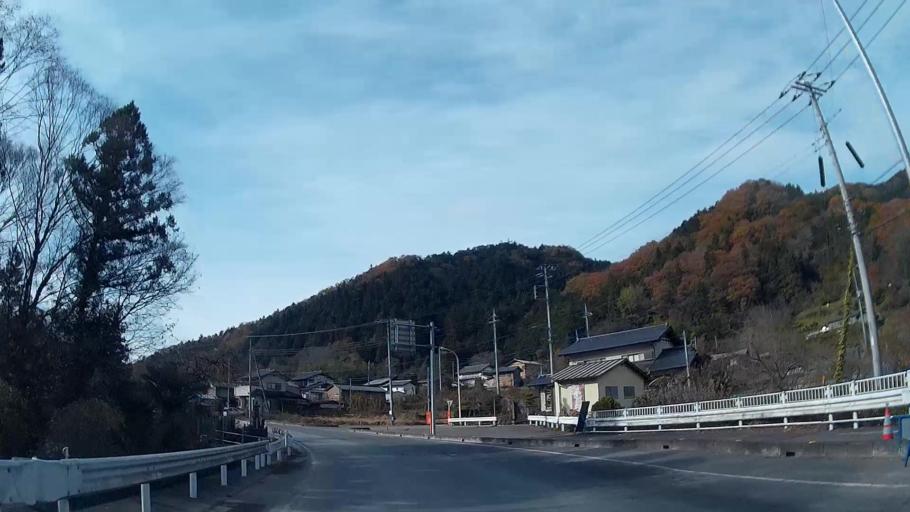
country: JP
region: Saitama
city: Chichibu
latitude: 36.0500
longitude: 139.0059
